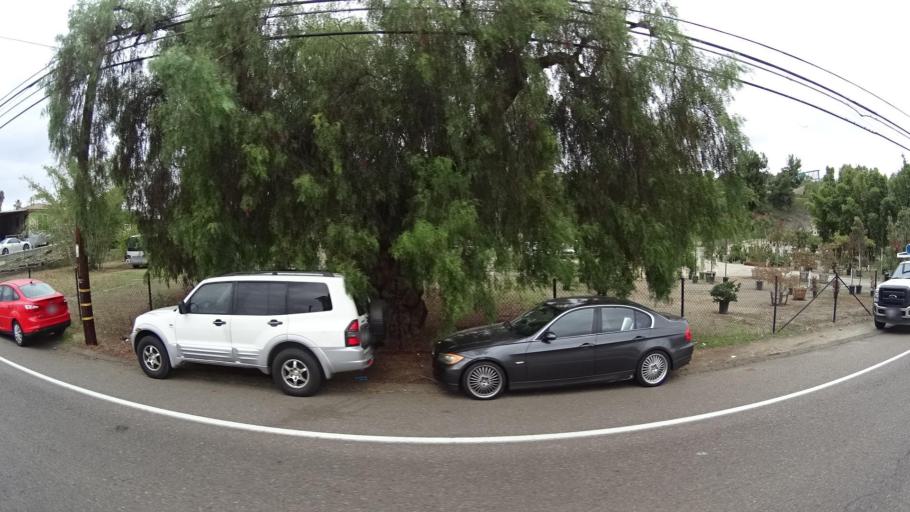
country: US
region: California
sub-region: San Diego County
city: Spring Valley
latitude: 32.7379
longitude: -117.0145
